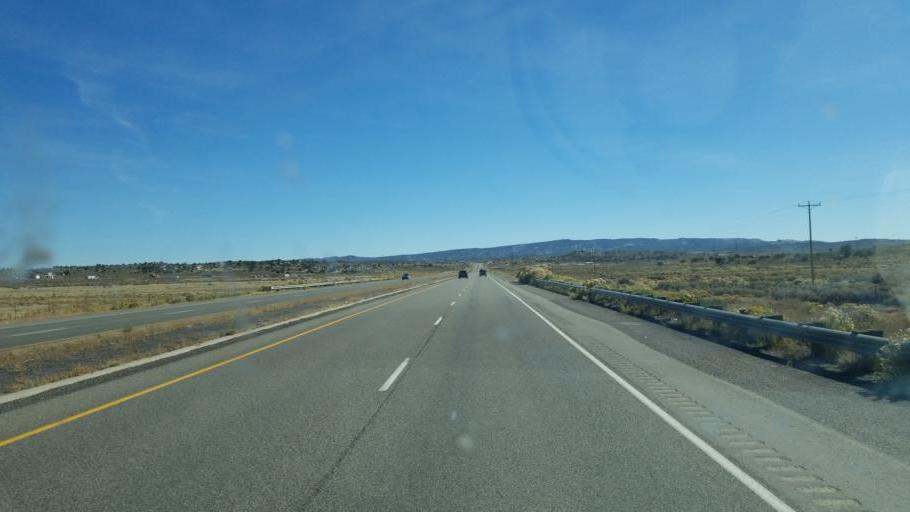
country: US
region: New Mexico
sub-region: McKinley County
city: Twin Lakes
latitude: 35.6342
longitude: -108.8199
